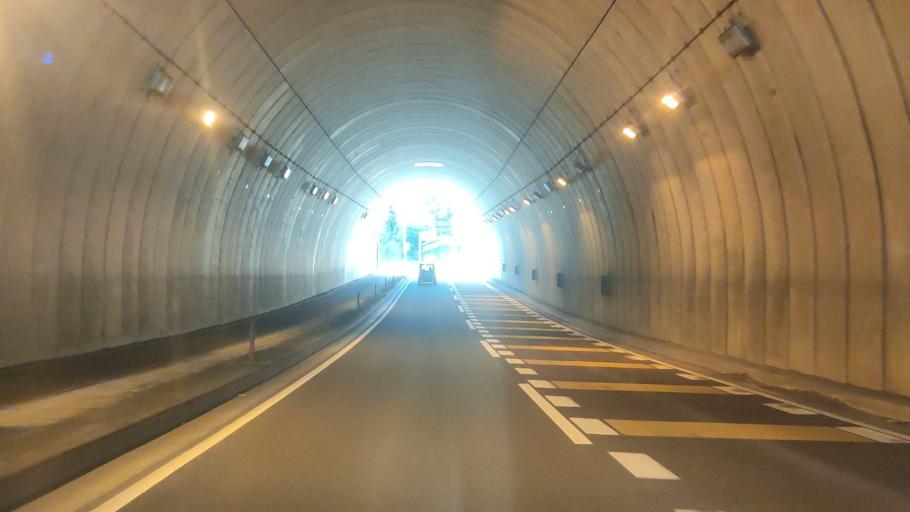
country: JP
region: Oita
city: Saiki
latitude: 32.9742
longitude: 131.8632
